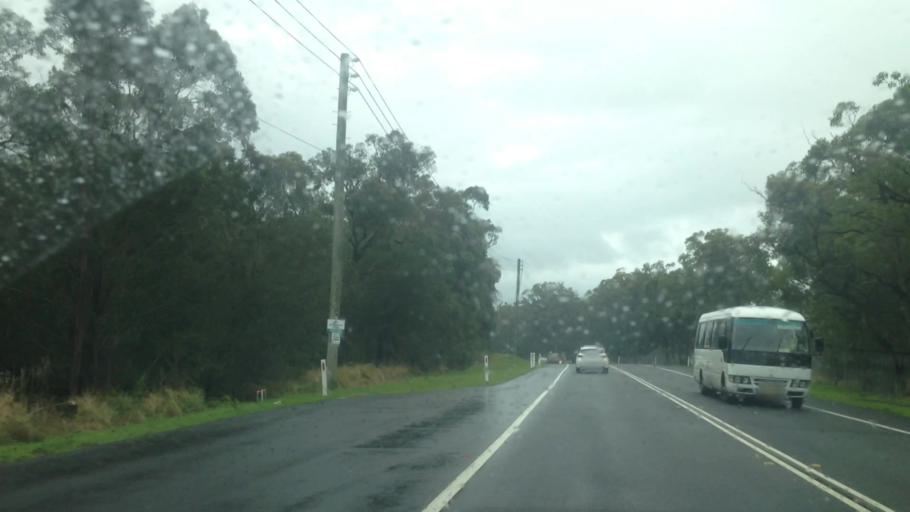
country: AU
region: New South Wales
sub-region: Lake Macquarie Shire
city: Dora Creek
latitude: -33.1215
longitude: 151.4768
